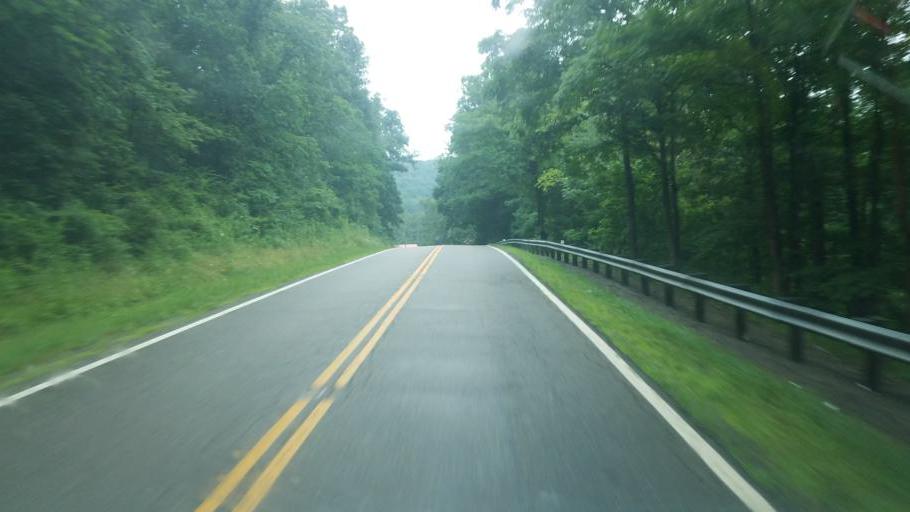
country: US
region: Ohio
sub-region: Carroll County
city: Carrollton
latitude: 40.4609
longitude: -80.9440
